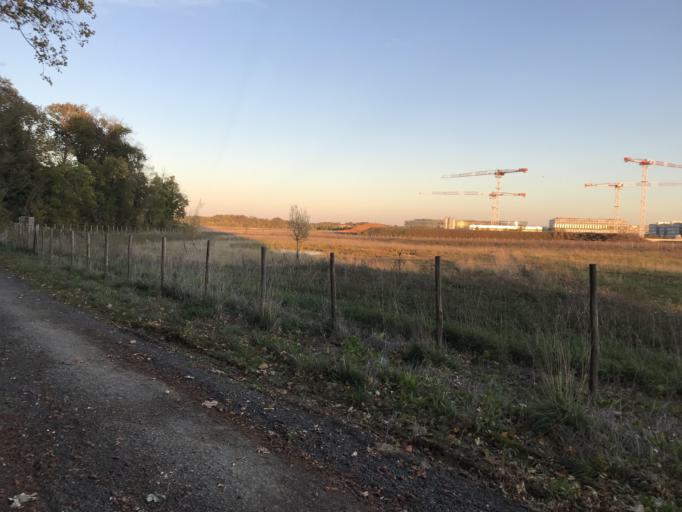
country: FR
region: Ile-de-France
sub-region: Departement de l'Essonne
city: Saclay
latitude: 48.7179
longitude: 2.1853
